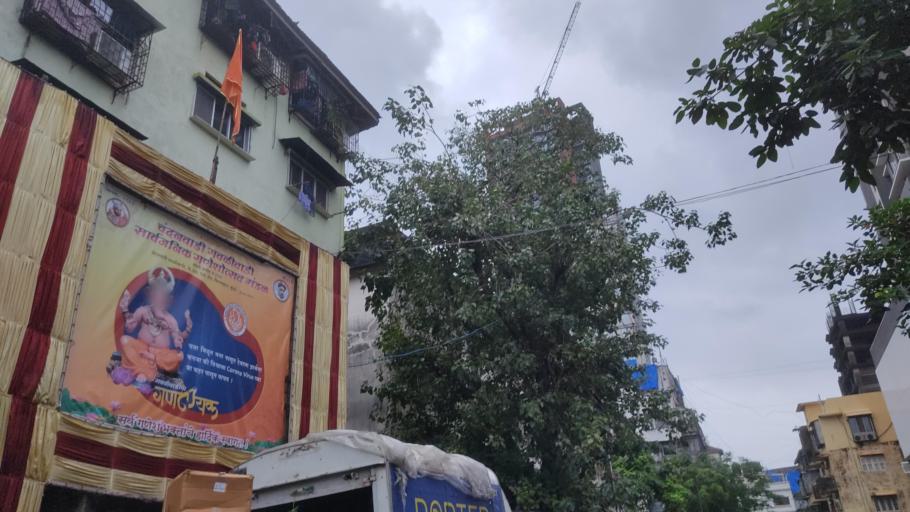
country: IN
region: Maharashtra
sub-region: Raigarh
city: Uran
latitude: 18.9463
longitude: 72.8261
